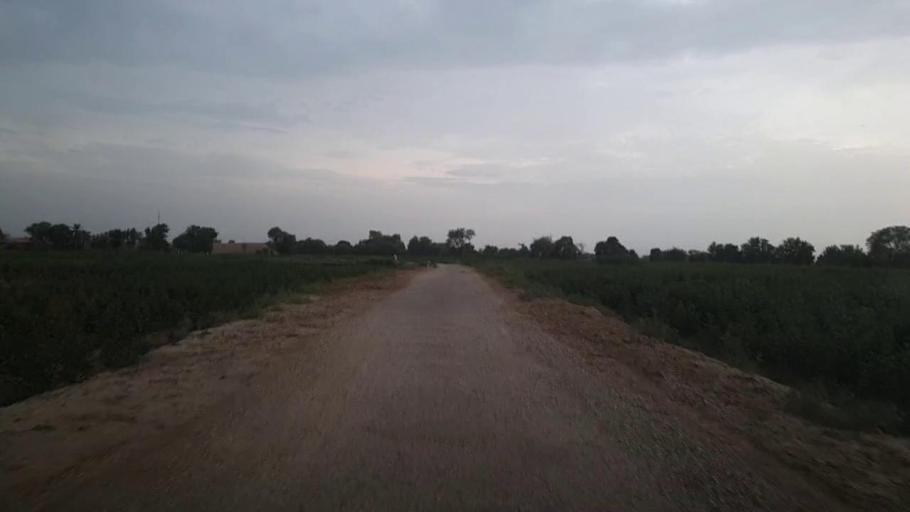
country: PK
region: Sindh
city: Karaundi
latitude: 27.0118
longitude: 68.3440
